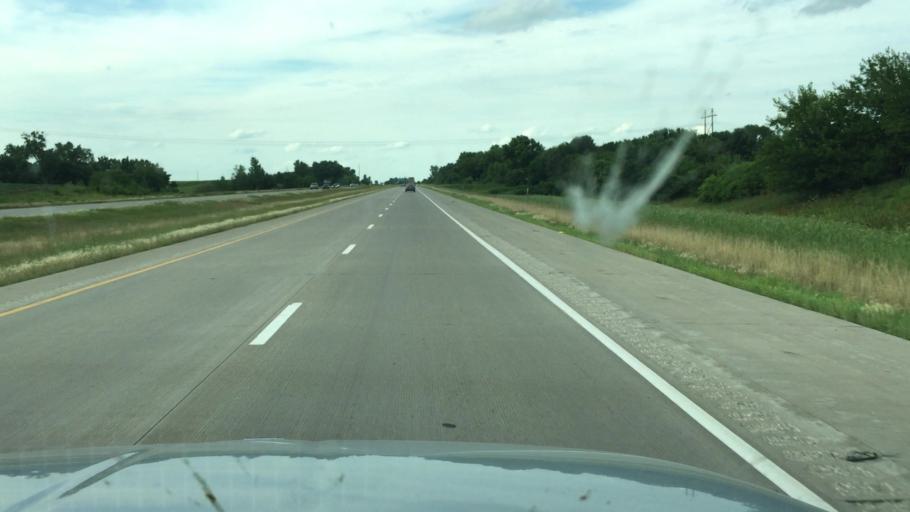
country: US
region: Iowa
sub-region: Scott County
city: Walcott
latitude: 41.5722
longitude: -90.6779
